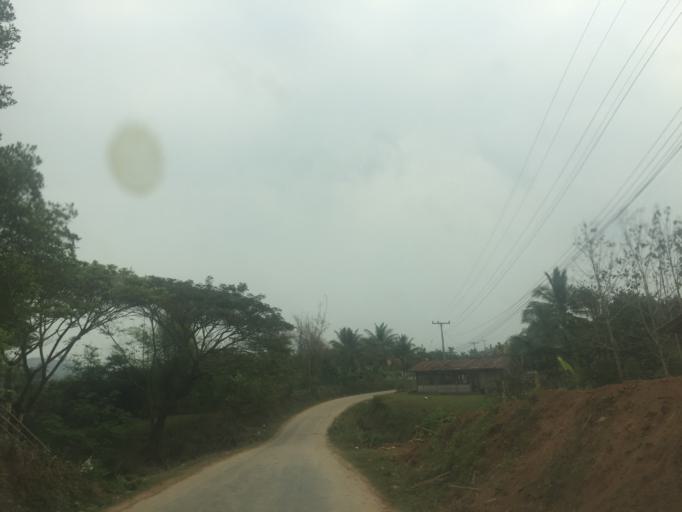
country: LA
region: Vientiane
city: Muang Sanakham
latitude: 18.3864
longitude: 101.5312
